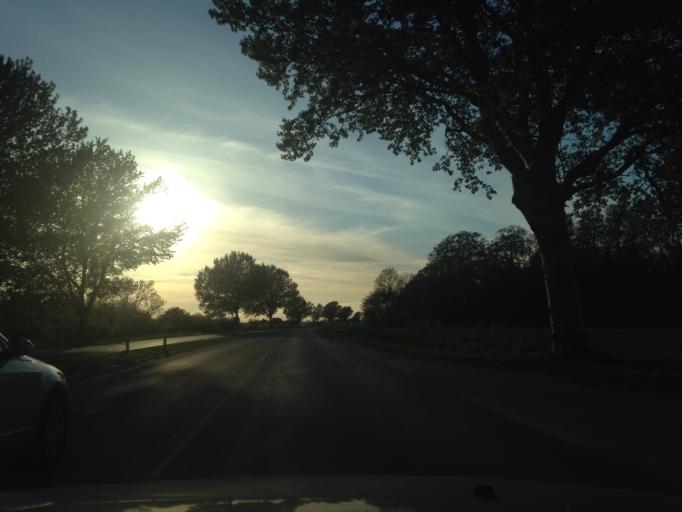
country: DK
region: Zealand
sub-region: Greve Kommune
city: Greve
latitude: 55.5901
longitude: 12.2455
